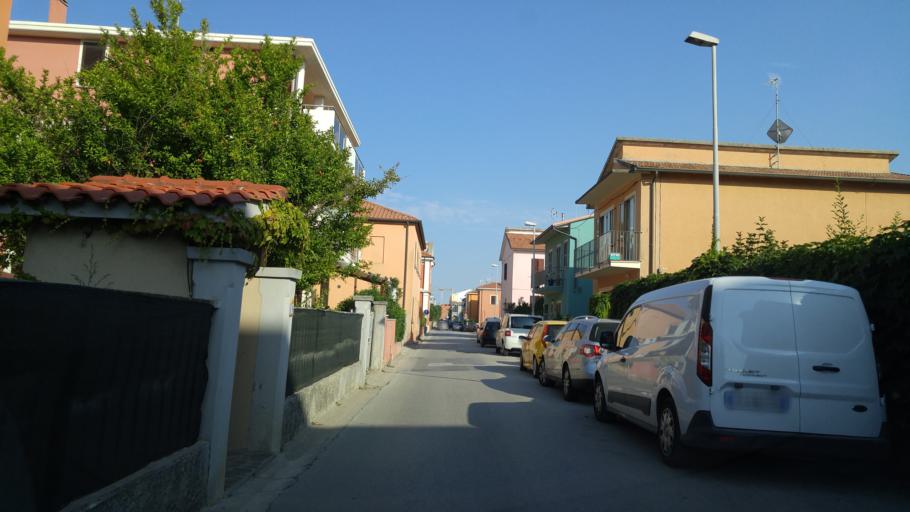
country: IT
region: The Marches
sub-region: Provincia di Pesaro e Urbino
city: Marotta
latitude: 43.7760
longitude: 13.1279
